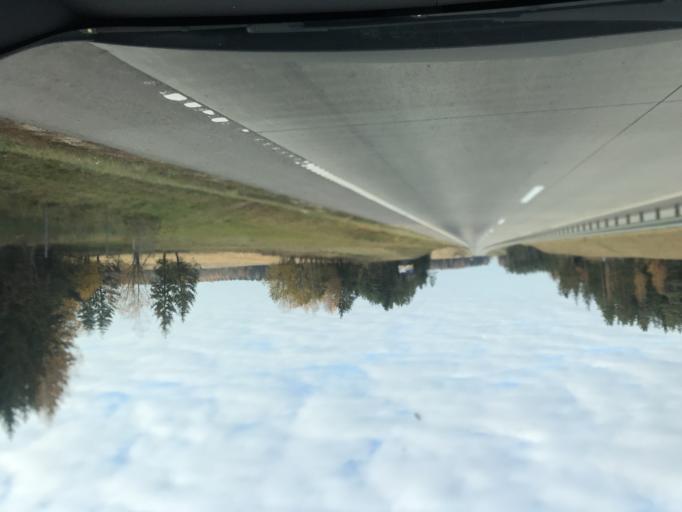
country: BY
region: Minsk
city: Rakaw
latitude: 53.9992
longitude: 27.1207
